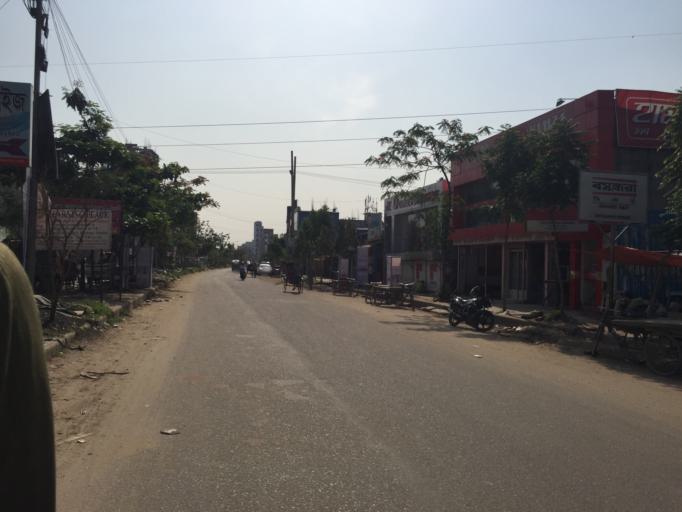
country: BD
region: Dhaka
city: Paltan
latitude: 23.7988
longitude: 90.4350
